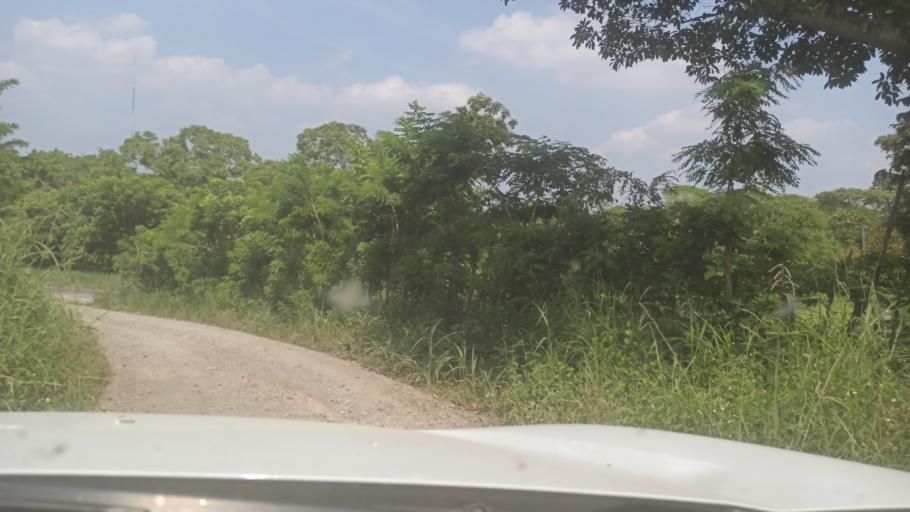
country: MX
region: Veracruz
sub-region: Atzalan
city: Colonias Pedernales
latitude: 20.0444
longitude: -97.0045
